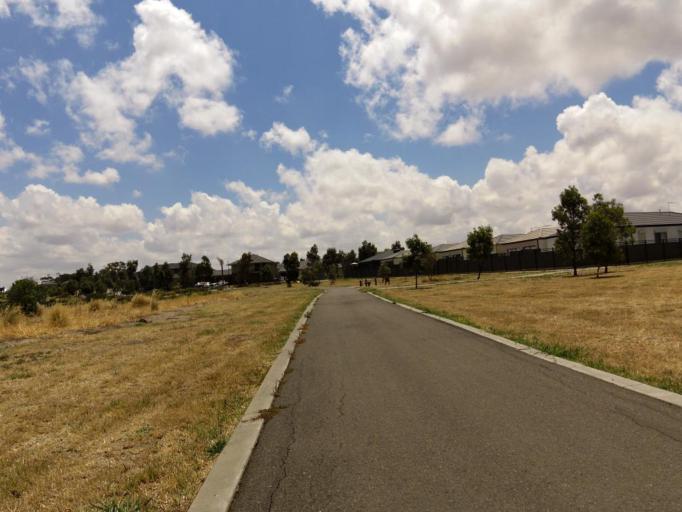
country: AU
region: Victoria
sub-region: Hume
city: Craigieburn
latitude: -37.5726
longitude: 144.9163
